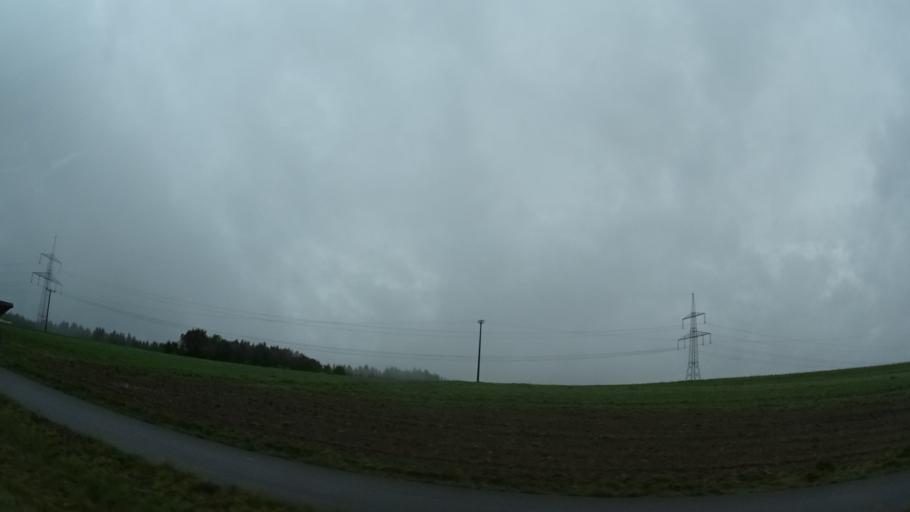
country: DE
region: Bavaria
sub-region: Upper Franconia
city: Wilhelmsthal
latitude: 50.3490
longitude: 11.4056
